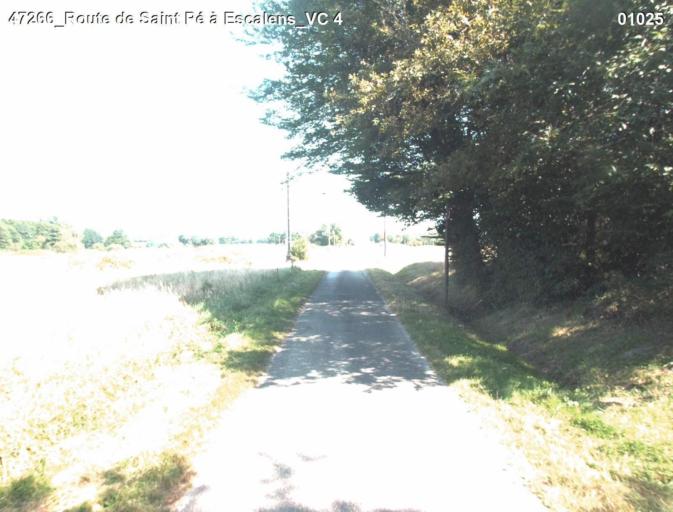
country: FR
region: Aquitaine
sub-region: Departement des Landes
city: Gabarret
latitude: 44.0017
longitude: 0.0728
